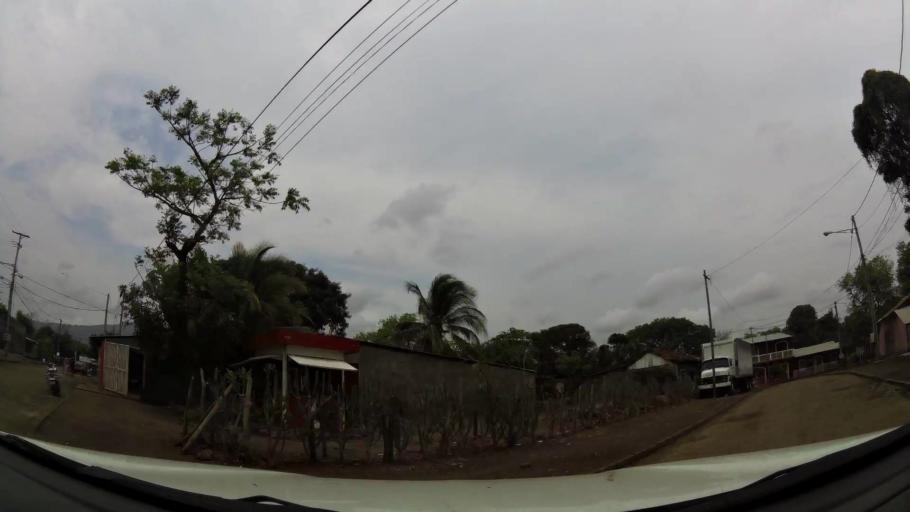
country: NI
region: Granada
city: Granada
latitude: 11.9142
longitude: -85.9554
